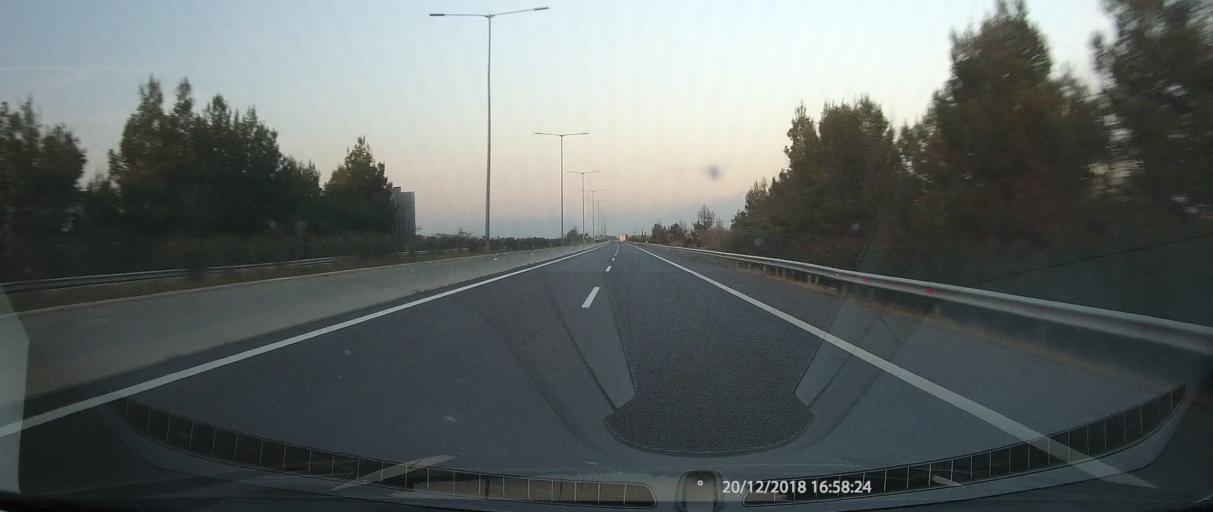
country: GR
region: Thessaly
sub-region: Nomos Larisis
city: Nikaia
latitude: 39.5939
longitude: 22.4911
